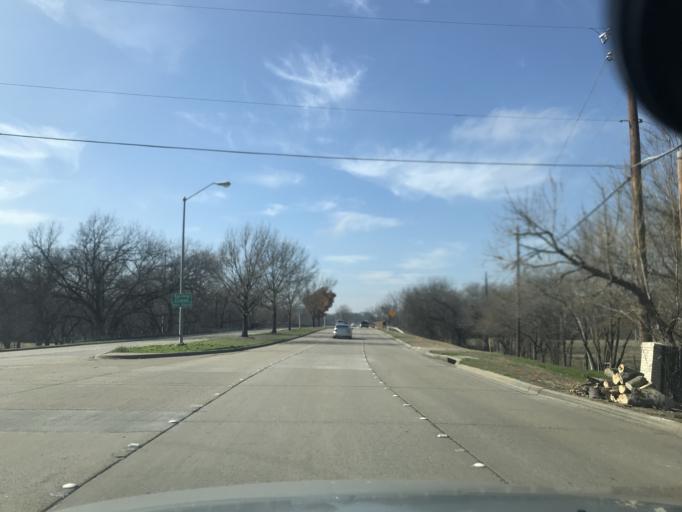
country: US
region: Texas
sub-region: Collin County
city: Parker
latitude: 33.0432
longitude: -96.6622
